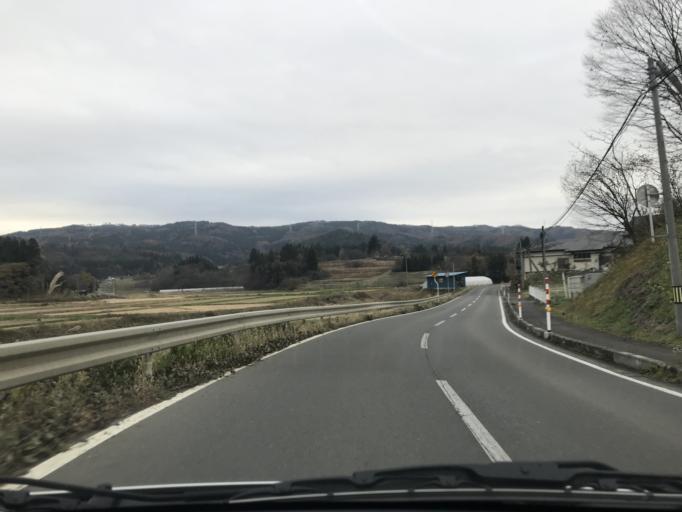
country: JP
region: Iwate
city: Kitakami
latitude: 39.2827
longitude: 141.2653
